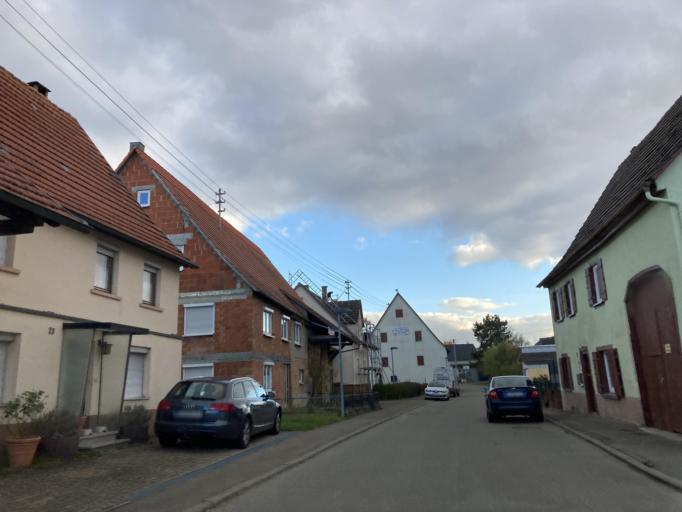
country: DE
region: Baden-Wuerttemberg
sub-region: Tuebingen Region
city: Haigerloch
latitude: 48.4297
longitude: 8.7856
